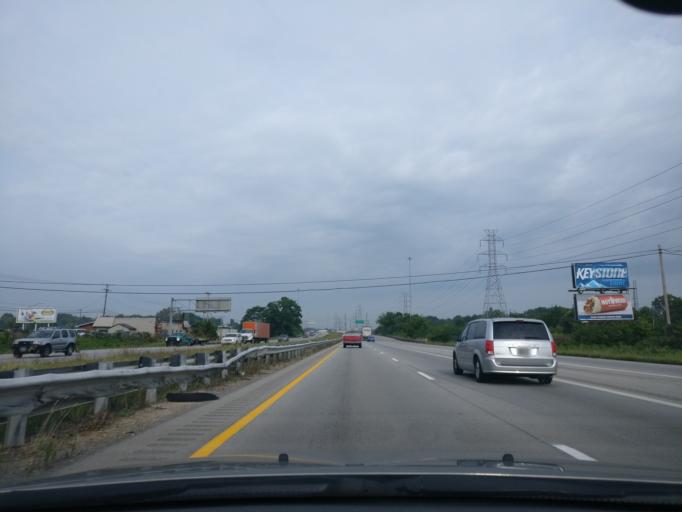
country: US
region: Ohio
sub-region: Montgomery County
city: Riverside
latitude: 39.7468
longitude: -84.1237
